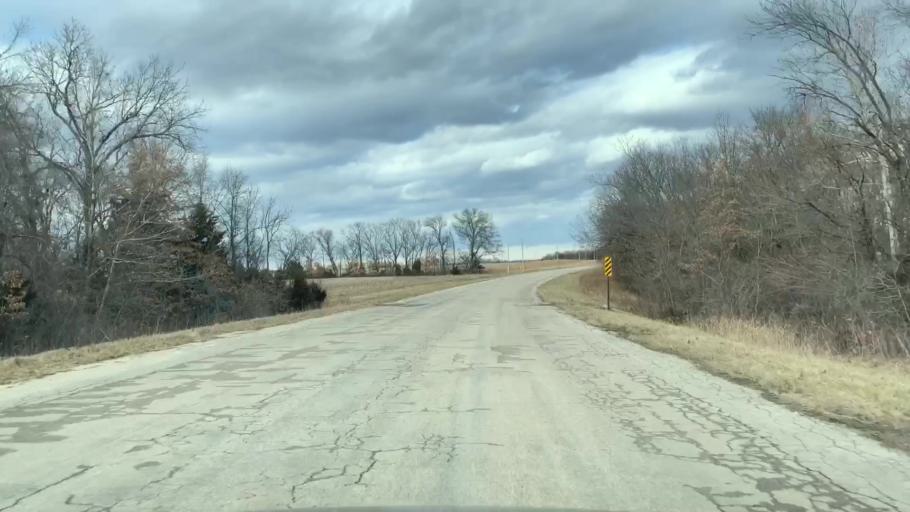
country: US
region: Kansas
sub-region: Allen County
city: Humboldt
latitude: 37.7569
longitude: -95.4719
